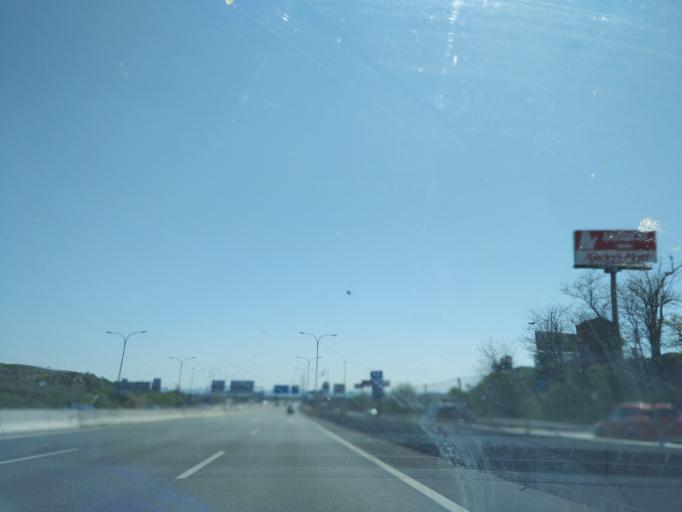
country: ES
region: Madrid
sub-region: Provincia de Madrid
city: Villa de Vallecas
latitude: 40.3655
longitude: -3.5760
